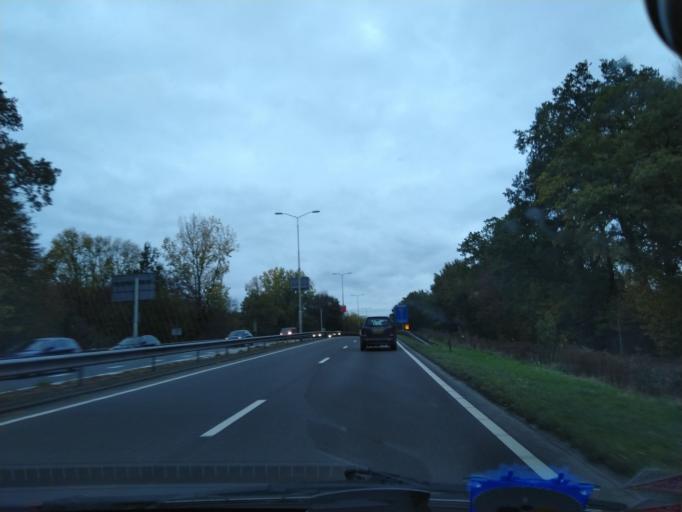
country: NL
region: Groningen
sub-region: Gemeente Groningen
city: Groningen
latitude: 53.2036
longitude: 6.5518
